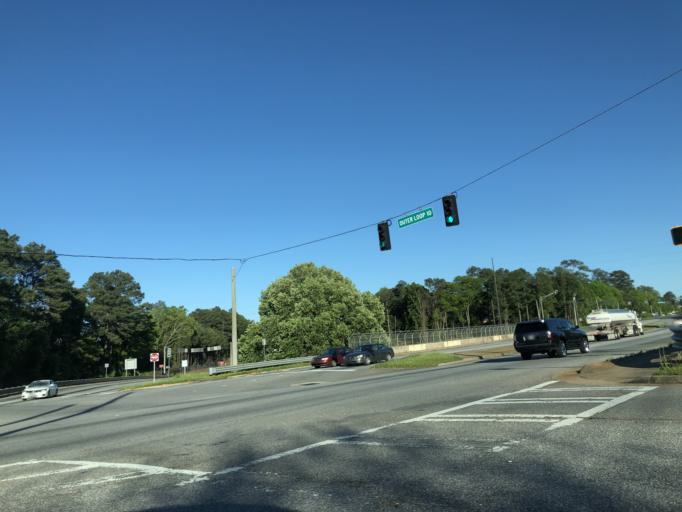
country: US
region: Georgia
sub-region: Clarke County
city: Country Club Estates
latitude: 33.9724
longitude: -83.4128
